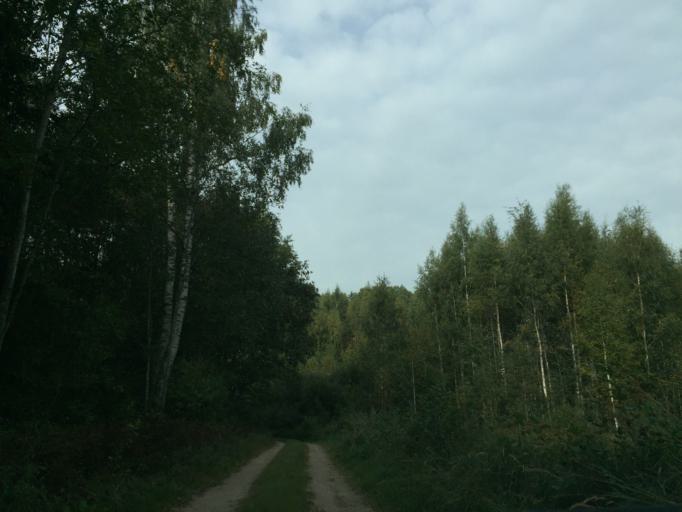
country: LV
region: Ikskile
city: Ikskile
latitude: 56.7594
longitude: 24.4752
